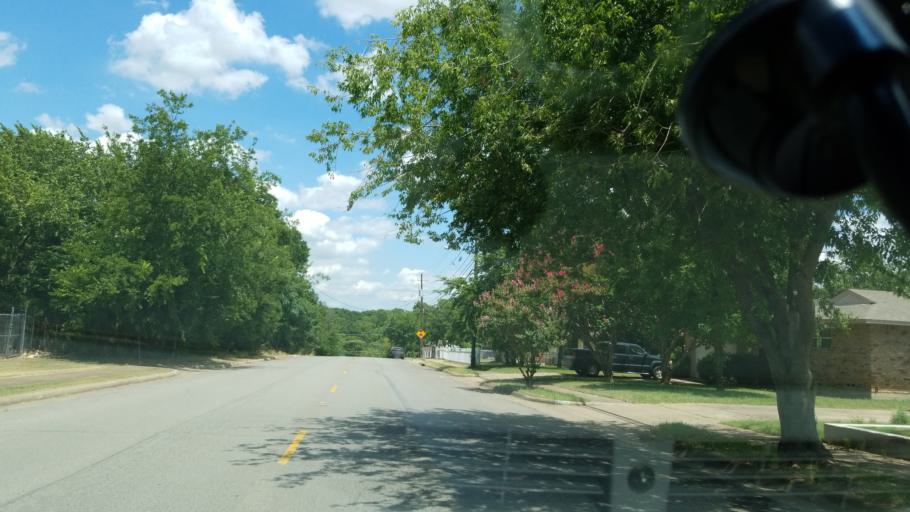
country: US
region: Texas
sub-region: Dallas County
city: Cockrell Hill
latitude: 32.6982
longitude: -96.8594
